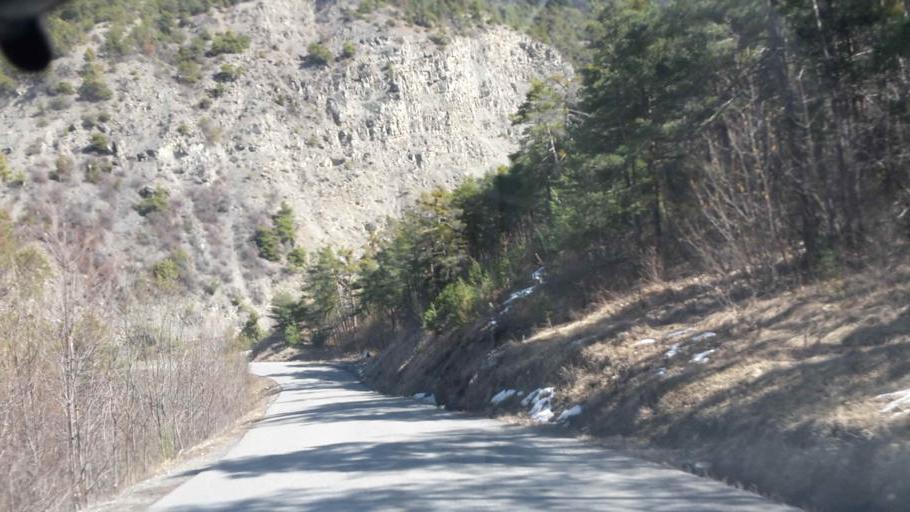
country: FR
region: Provence-Alpes-Cote d'Azur
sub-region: Departement des Hautes-Alpes
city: Embrun
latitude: 44.5607
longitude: 6.5513
